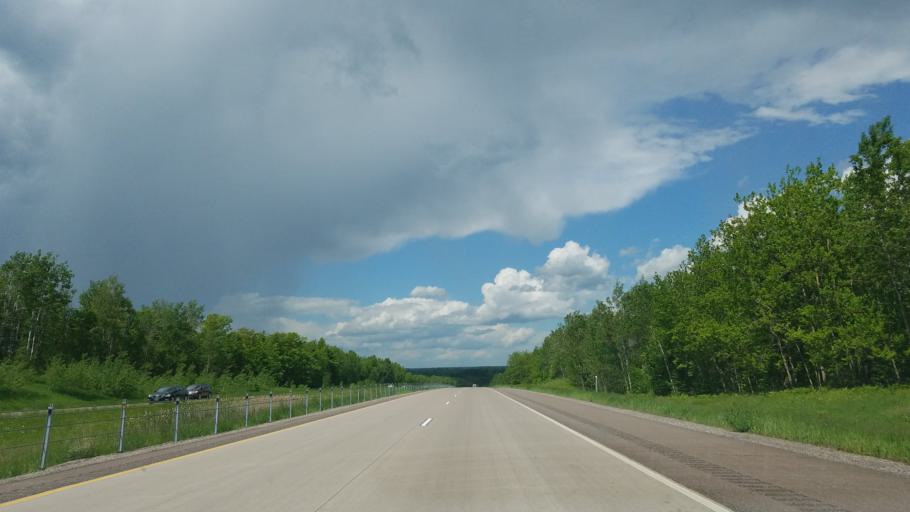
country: US
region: Minnesota
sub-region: Carlton County
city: Moose Lake
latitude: 46.4679
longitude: -92.7182
